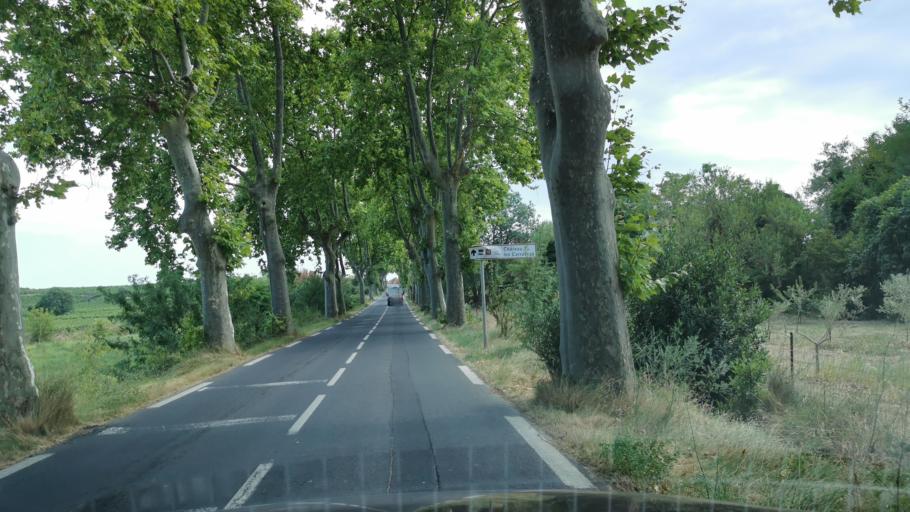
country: FR
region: Languedoc-Roussillon
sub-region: Departement de l'Herault
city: Puisserguier
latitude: 43.3606
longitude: 3.0394
